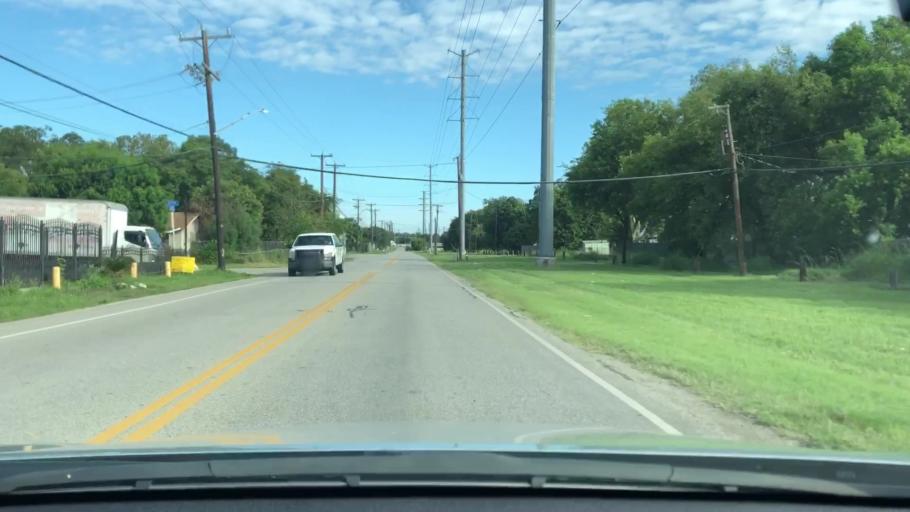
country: US
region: Texas
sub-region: Bexar County
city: Windcrest
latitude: 29.4917
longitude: -98.3927
